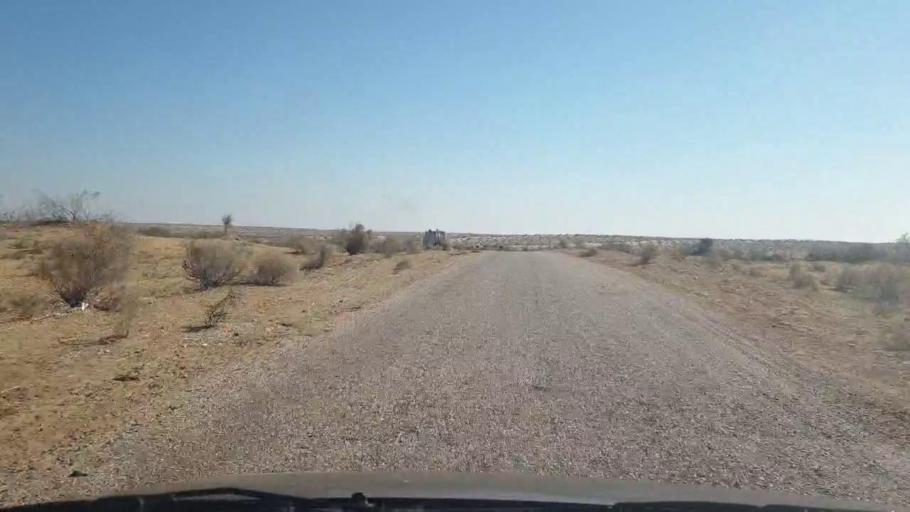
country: PK
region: Sindh
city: Bozdar
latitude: 27.0015
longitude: 68.8082
